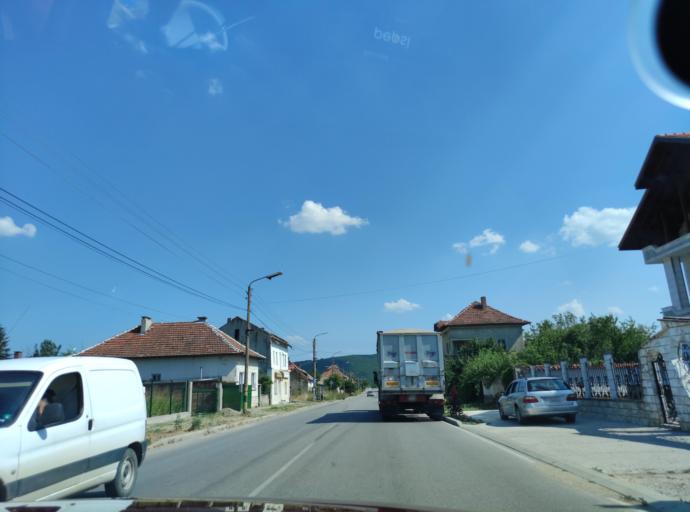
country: BG
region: Pleven
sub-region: Obshtina Cherven Bryag
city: Cherven Bryag
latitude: 43.3265
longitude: 24.0681
